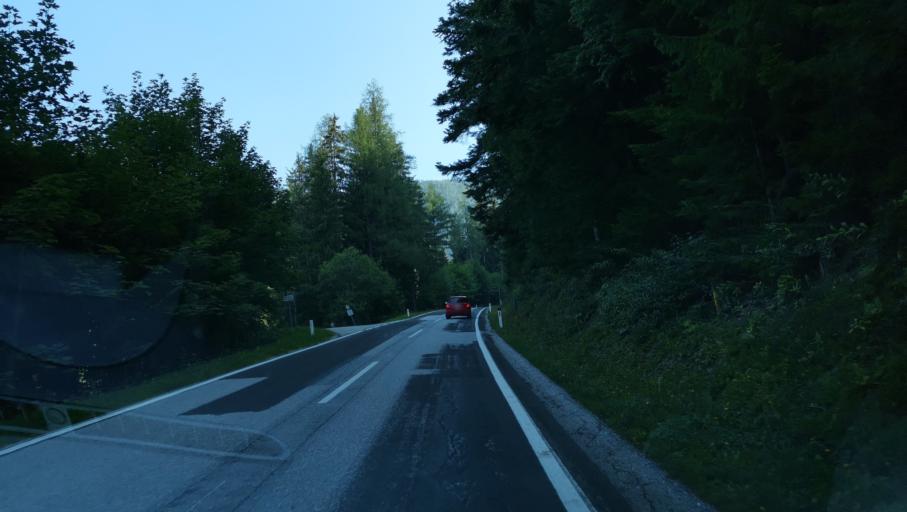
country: AT
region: Styria
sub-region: Politischer Bezirk Liezen
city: Trieben
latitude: 47.5207
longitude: 14.4438
